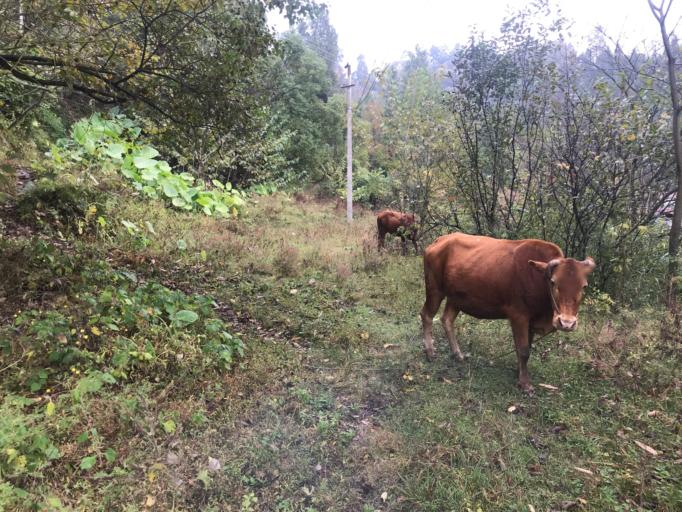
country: CN
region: Guizhou Sheng
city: Xujiaba
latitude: 27.8860
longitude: 108.1845
